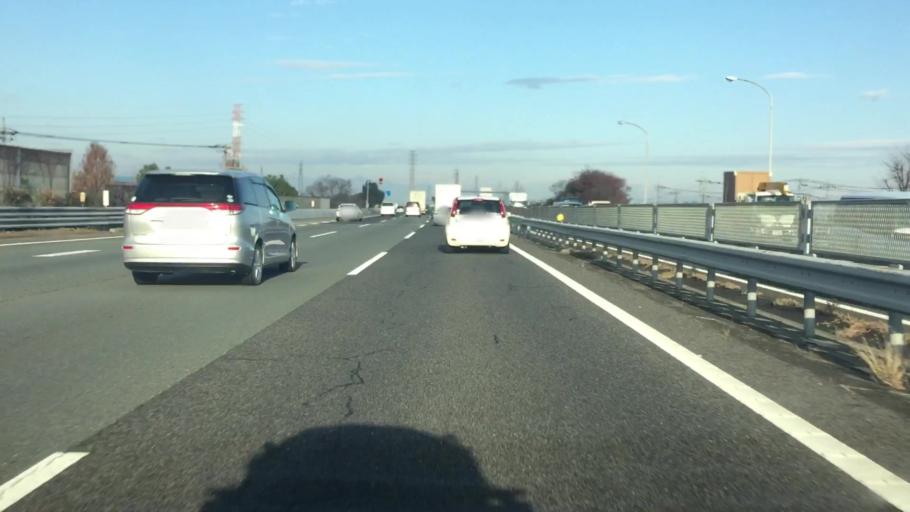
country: JP
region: Saitama
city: Honjo
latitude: 36.2200
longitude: 139.1634
